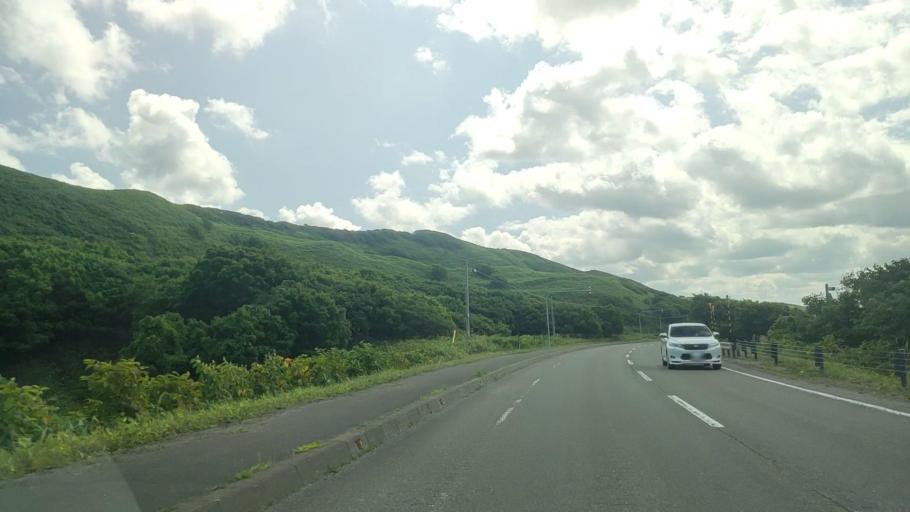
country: JP
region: Hokkaido
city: Wakkanai
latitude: 45.3681
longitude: 141.6615
